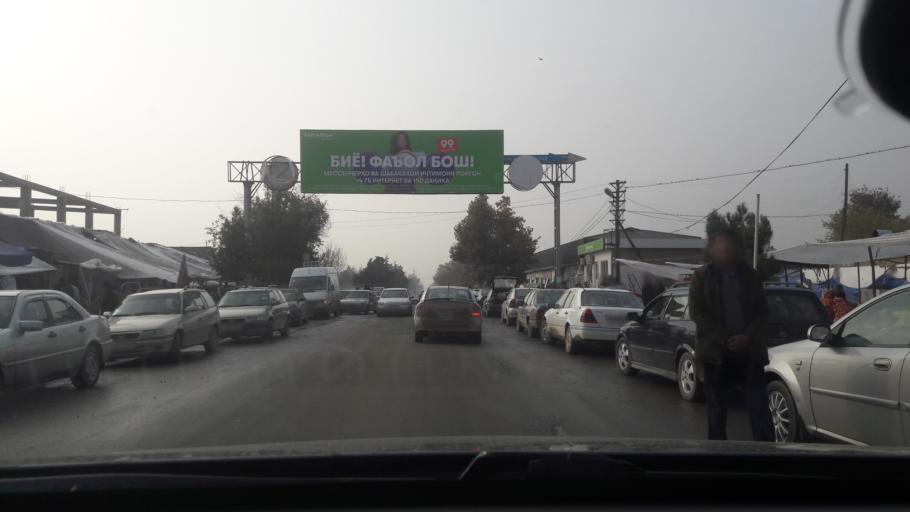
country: TJ
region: Khatlon
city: Abdurahmoni Jomi
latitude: 37.9794
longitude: 68.6943
